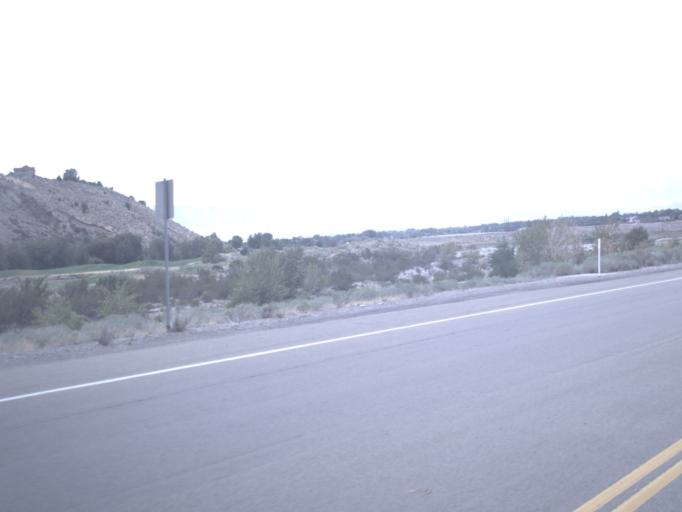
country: US
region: Utah
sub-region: Utah County
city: Cedar Hills
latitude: 40.4318
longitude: -111.7558
